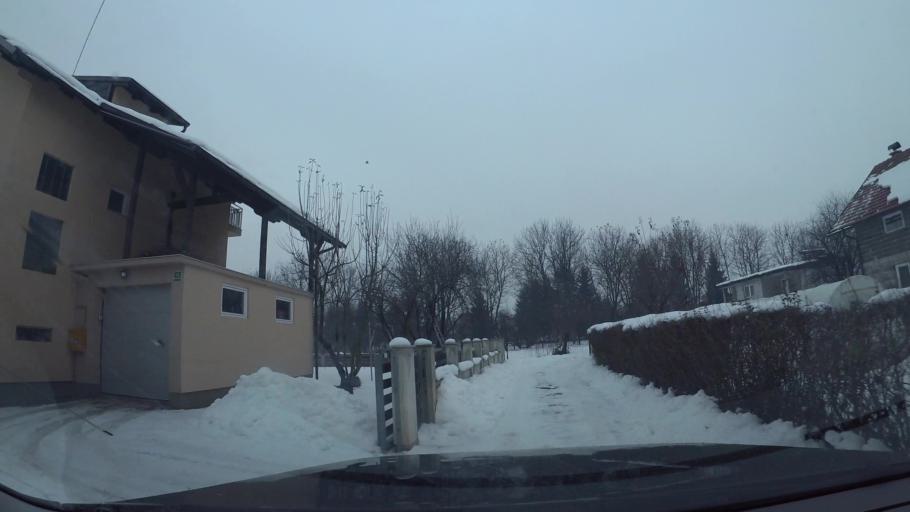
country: BA
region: Federation of Bosnia and Herzegovina
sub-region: Kanton Sarajevo
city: Sarajevo
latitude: 43.8417
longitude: 18.2940
